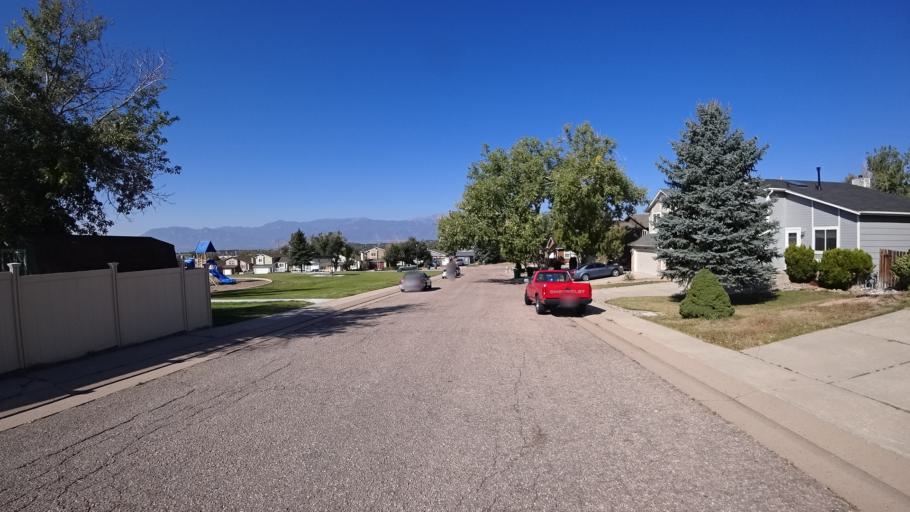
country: US
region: Colorado
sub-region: El Paso County
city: Cimarron Hills
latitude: 38.8707
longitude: -104.7075
